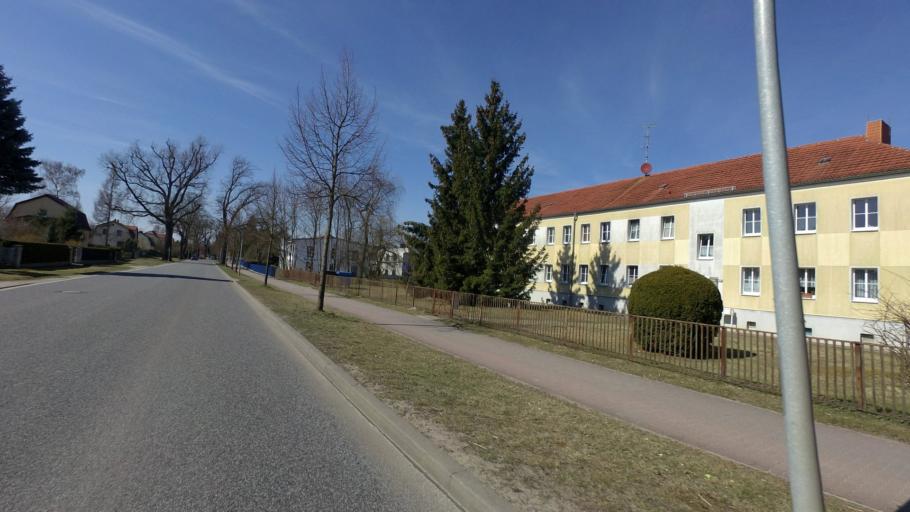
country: DE
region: Brandenburg
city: Muncheberg
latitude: 52.5111
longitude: 14.1219
